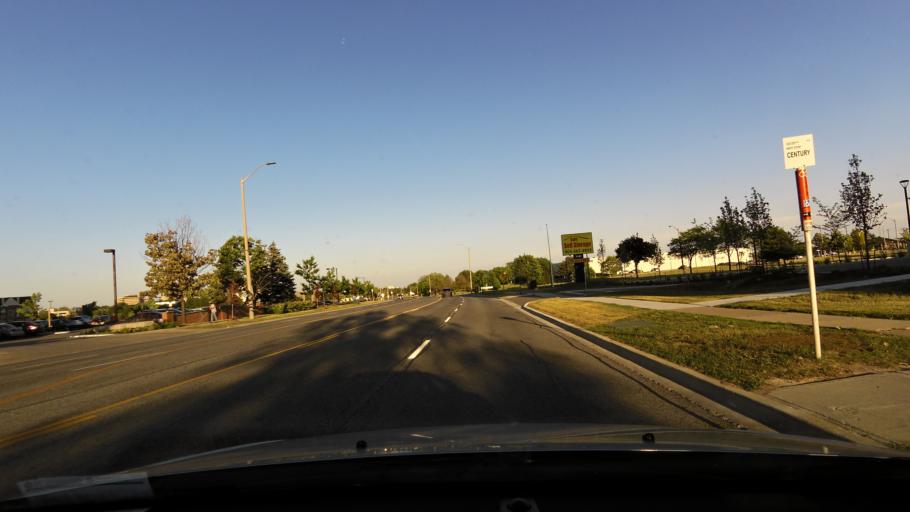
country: CA
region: Ontario
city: Brampton
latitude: 43.6010
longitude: -79.7560
